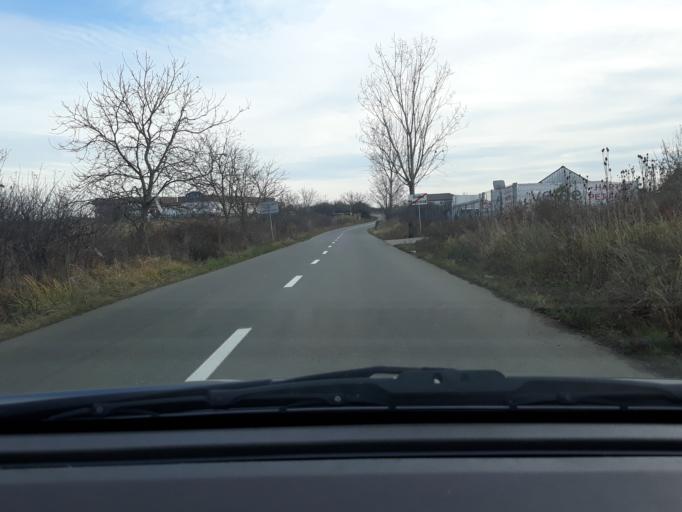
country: RO
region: Bihor
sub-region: Comuna Sanmartin
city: Sanmartin
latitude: 47.0305
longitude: 21.9971
